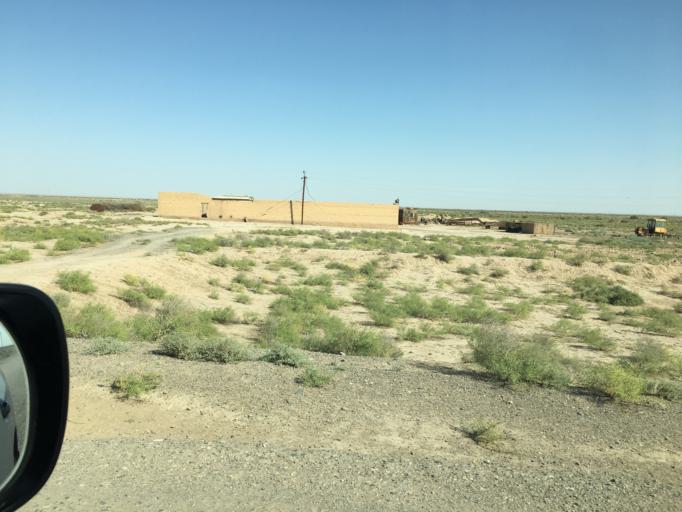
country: IR
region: Razavi Khorasan
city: Sarakhs
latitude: 36.6240
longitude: 61.3003
